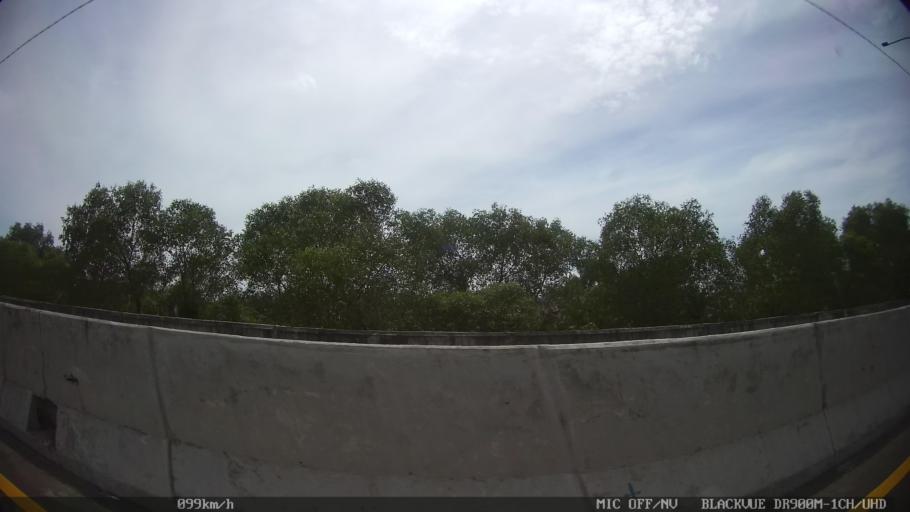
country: ID
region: North Sumatra
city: Belawan
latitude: 3.7534
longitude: 98.6823
